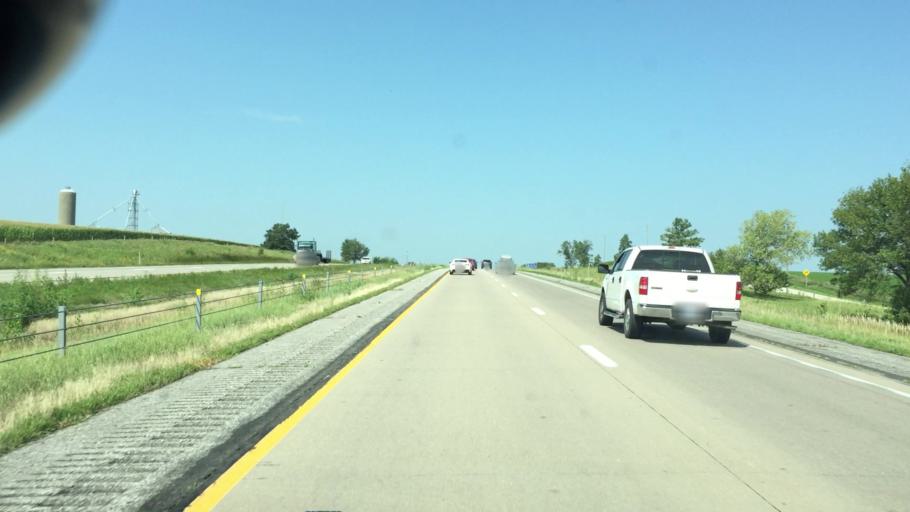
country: US
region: Iowa
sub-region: Iowa County
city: Williamsburg
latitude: 41.6873
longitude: -92.0317
